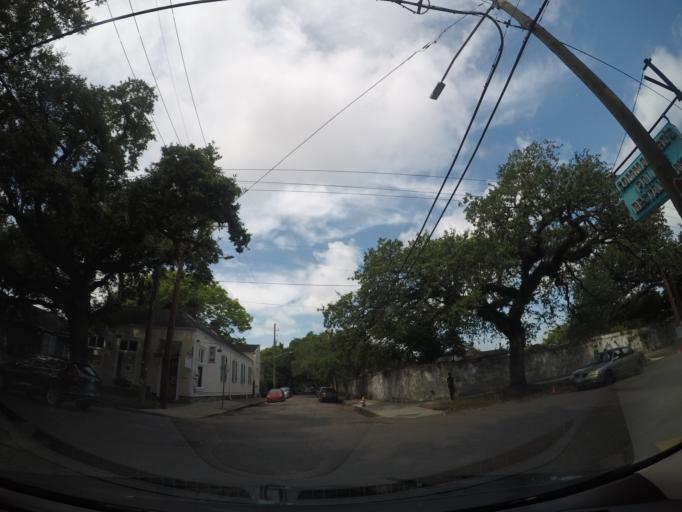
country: US
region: Louisiana
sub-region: Jefferson Parish
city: Harvey
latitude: 29.9287
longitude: -90.0841
